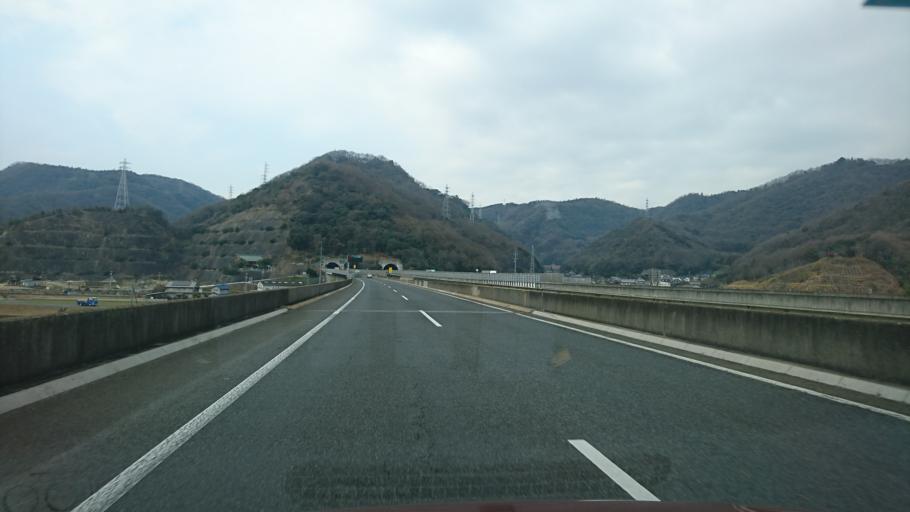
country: JP
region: Hiroshima
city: Fukuyama
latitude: 34.5125
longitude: 133.3469
